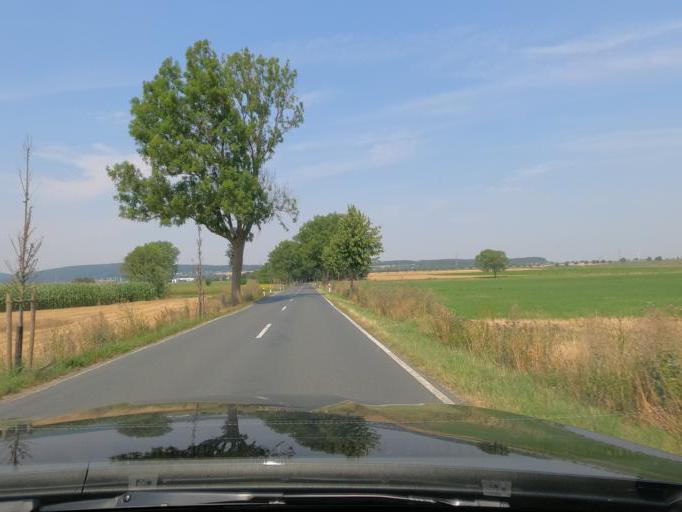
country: DE
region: Lower Saxony
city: Springe
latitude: 52.1957
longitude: 9.6360
